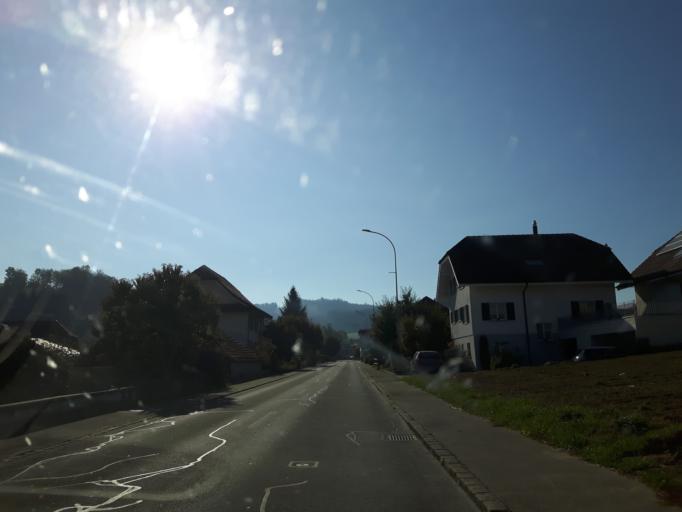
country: CH
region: Lucerne
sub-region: Willisau District
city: Pfaffnau
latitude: 47.2290
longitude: 7.8951
